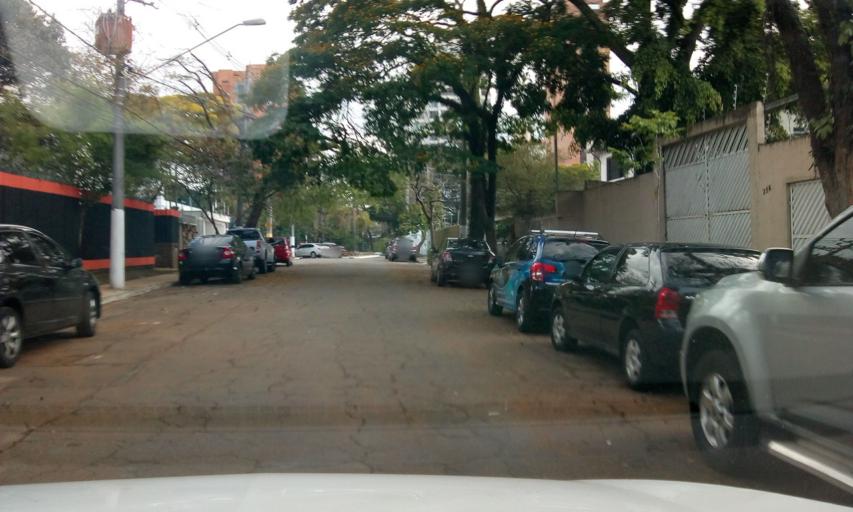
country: BR
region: Sao Paulo
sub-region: Sao Paulo
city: Sao Paulo
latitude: -23.6029
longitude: -46.6539
